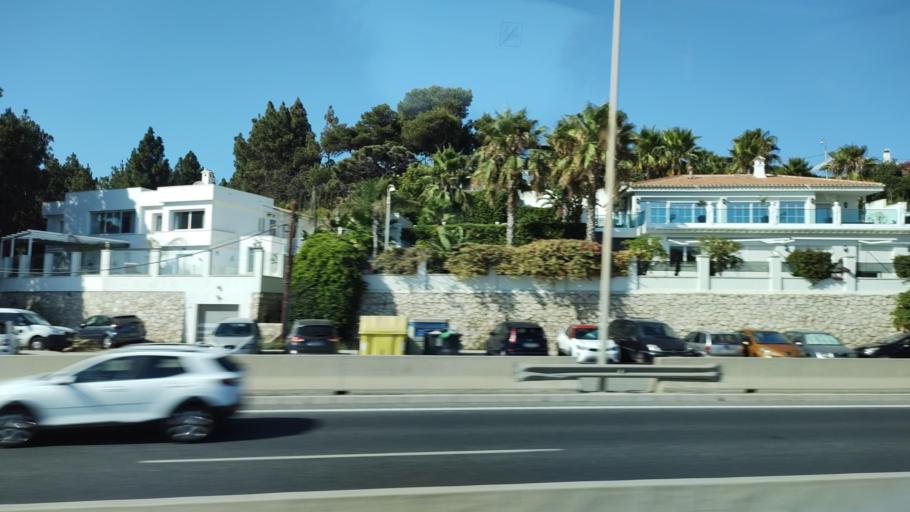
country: ES
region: Andalusia
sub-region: Provincia de Malaga
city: Fuengirola
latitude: 36.5073
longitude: -4.6613
